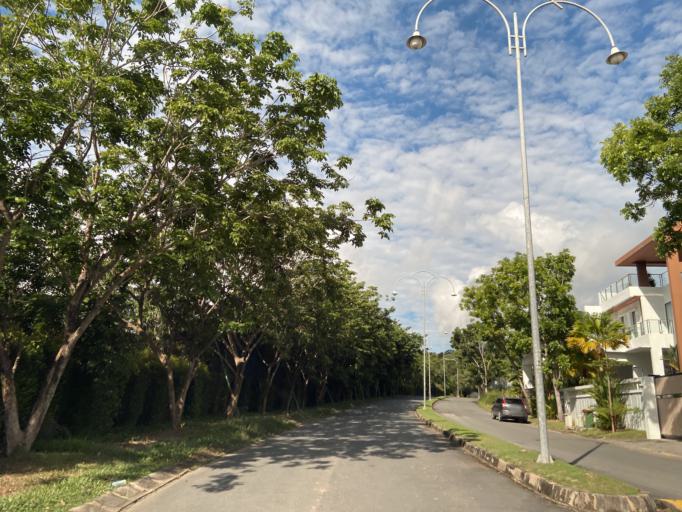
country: SG
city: Singapore
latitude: 1.0946
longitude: 104.0297
